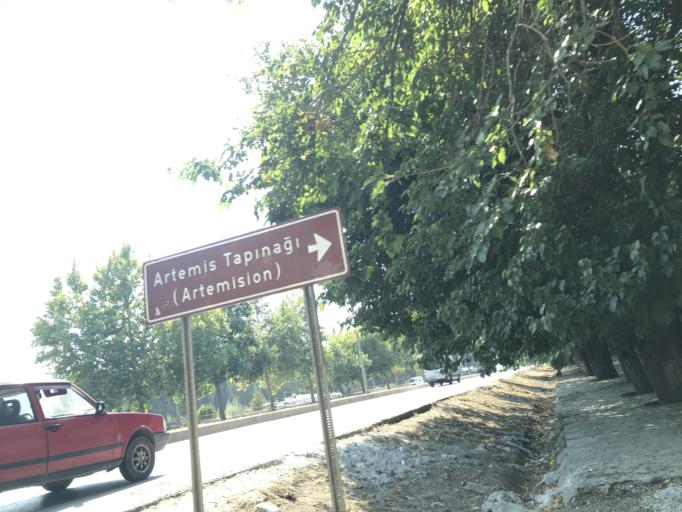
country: TR
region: Izmir
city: Selcuk
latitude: 37.9485
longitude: 27.3623
